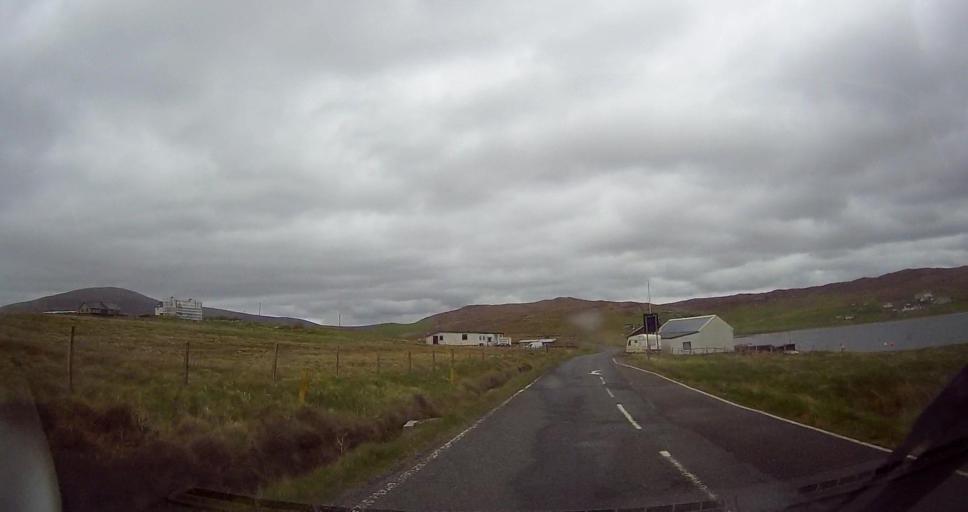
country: GB
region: Scotland
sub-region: Shetland Islands
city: Lerwick
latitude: 60.4893
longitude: -1.4654
